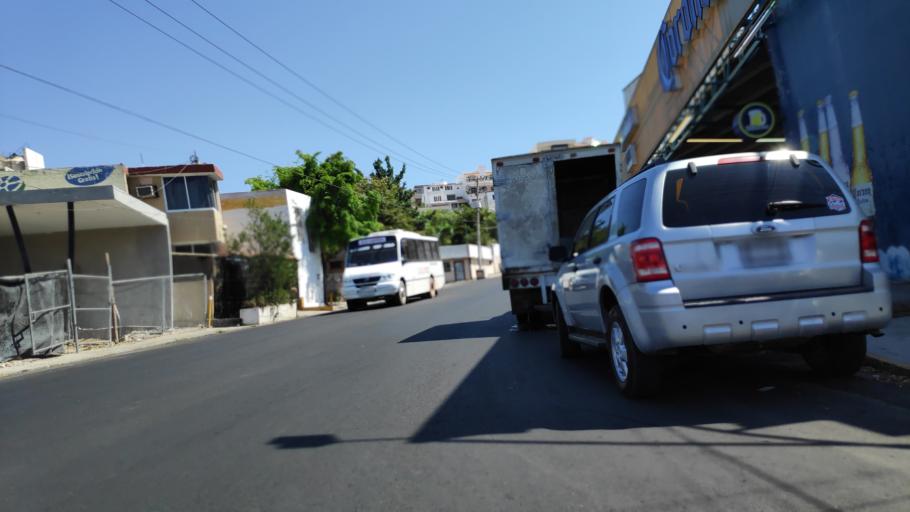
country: MX
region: Sinaloa
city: Culiacan
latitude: 24.7859
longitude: -107.4005
